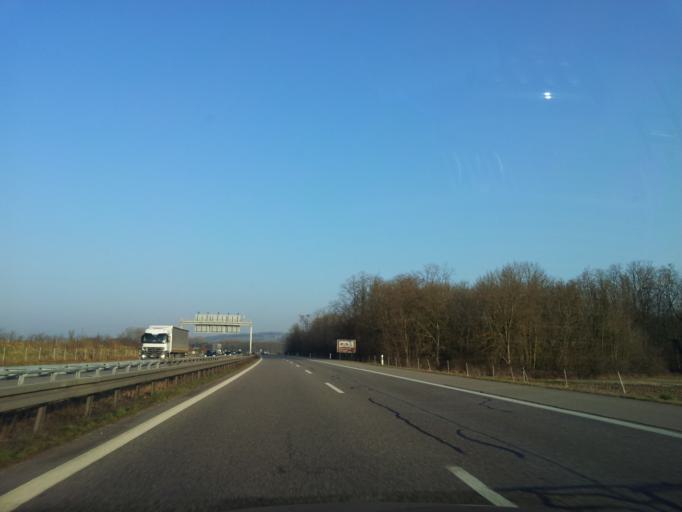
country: DE
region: Baden-Wuerttemberg
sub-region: Freiburg Region
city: Efringen-Kirchen
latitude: 47.6331
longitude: 7.5694
